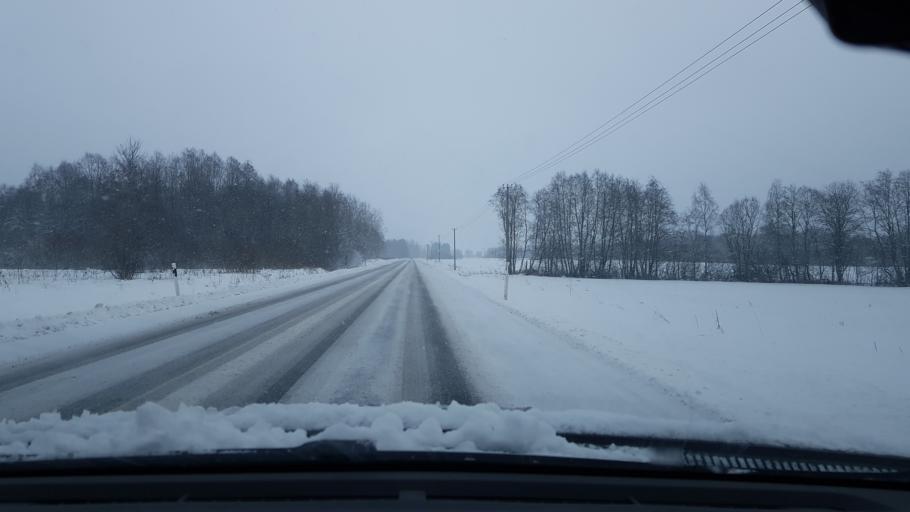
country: EE
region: Harju
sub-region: Joelaehtme vald
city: Loo
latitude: 59.3884
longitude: 24.9895
